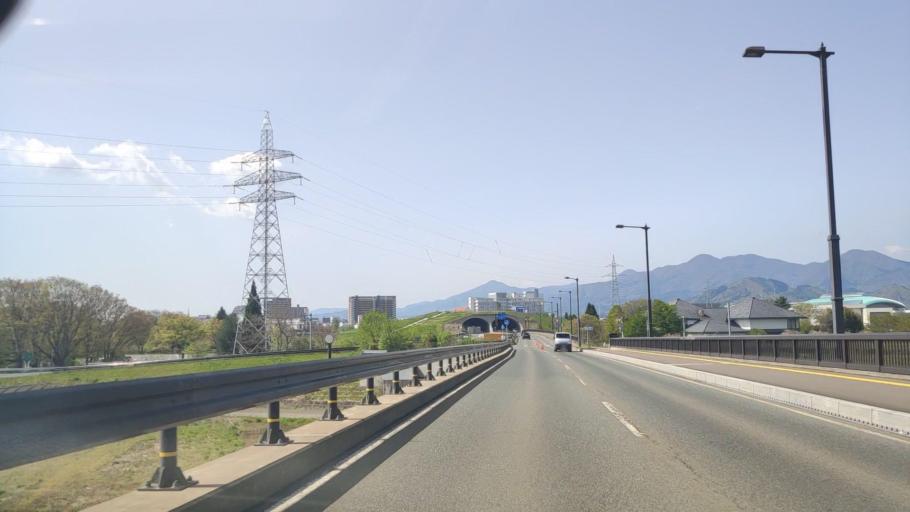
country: JP
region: Iwate
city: Morioka-shi
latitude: 39.6961
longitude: 141.1291
